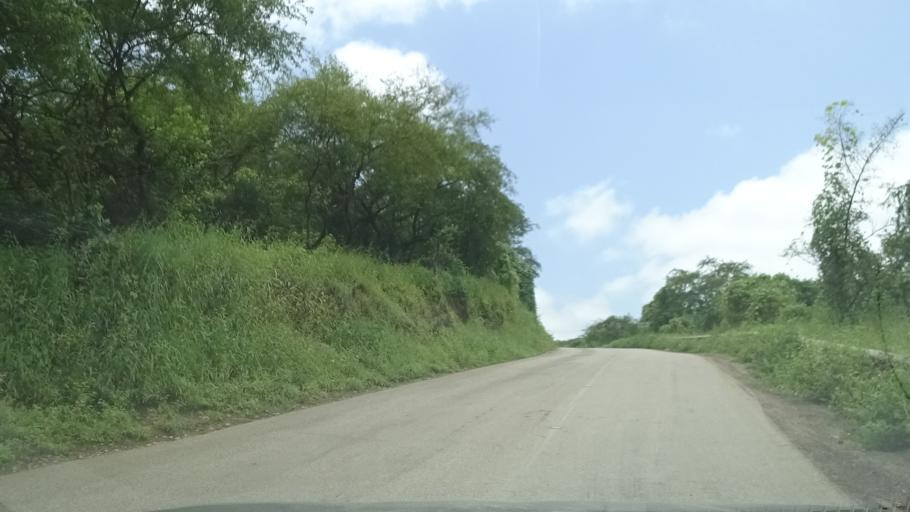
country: OM
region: Zufar
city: Salalah
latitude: 17.2001
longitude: 54.1812
